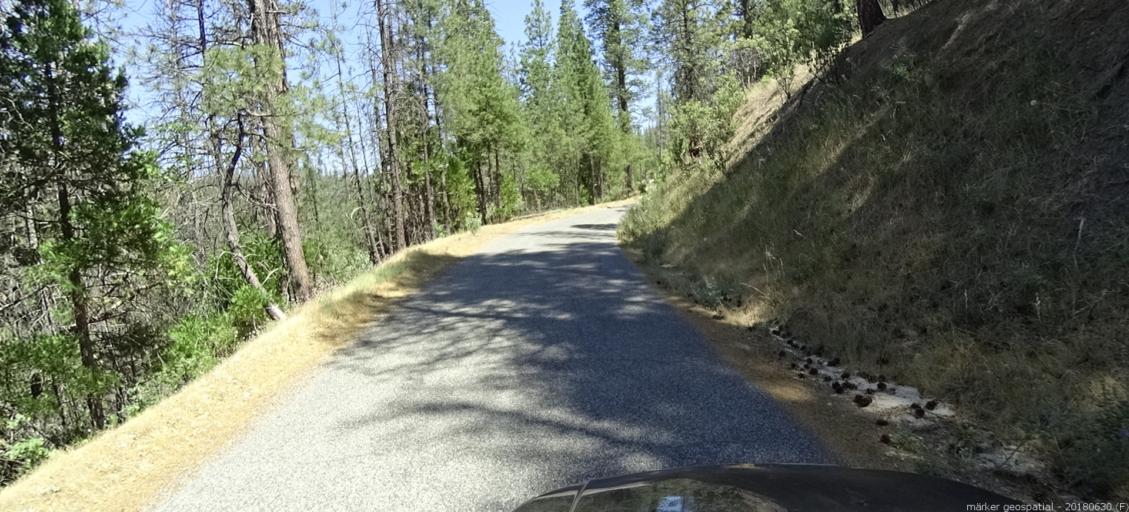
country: US
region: California
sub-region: Madera County
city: Oakhurst
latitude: 37.3659
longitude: -119.3526
